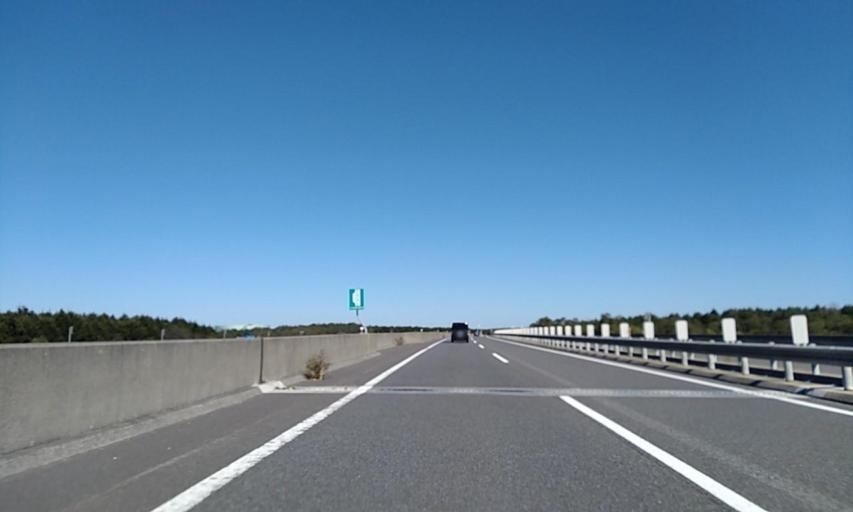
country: JP
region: Hokkaido
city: Tomakomai
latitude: 42.6345
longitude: 141.8331
